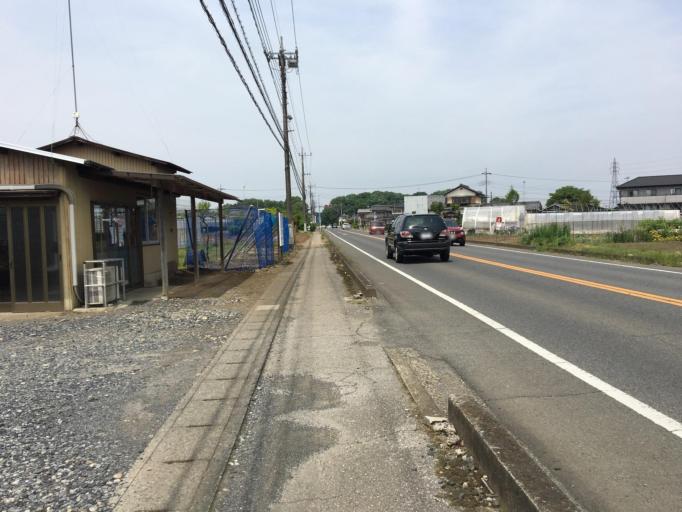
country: JP
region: Tochigi
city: Oyama
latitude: 36.3519
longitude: 139.8133
